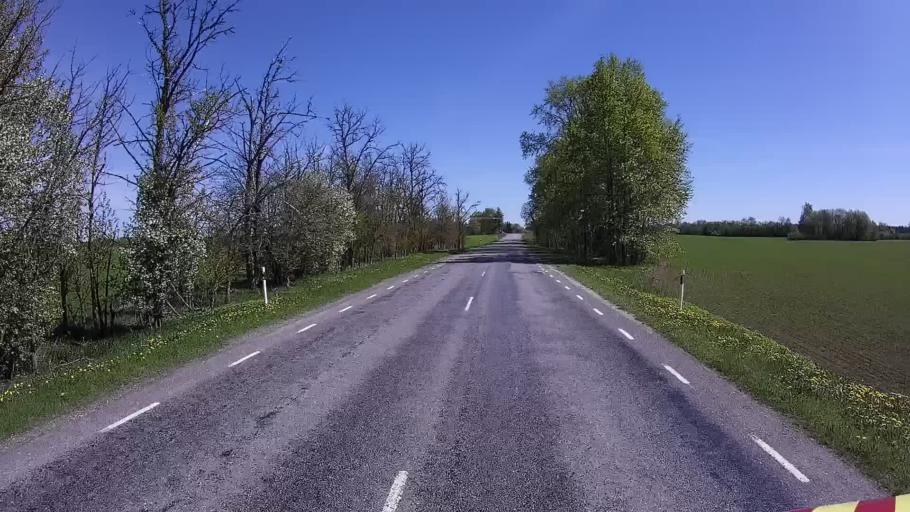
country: EE
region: Raplamaa
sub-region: Kehtna vald
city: Kehtna
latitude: 59.0552
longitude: 24.9881
